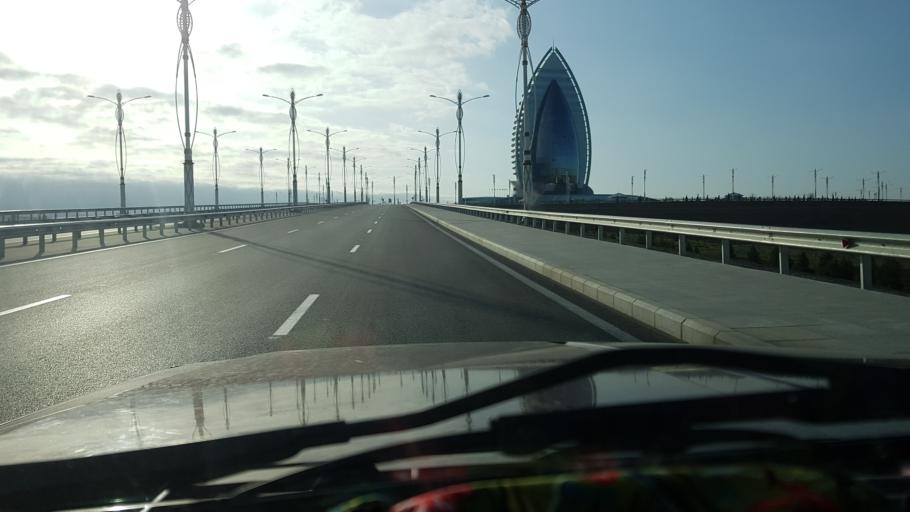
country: TM
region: Ahal
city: Ashgabat
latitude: 37.9273
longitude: 58.3387
